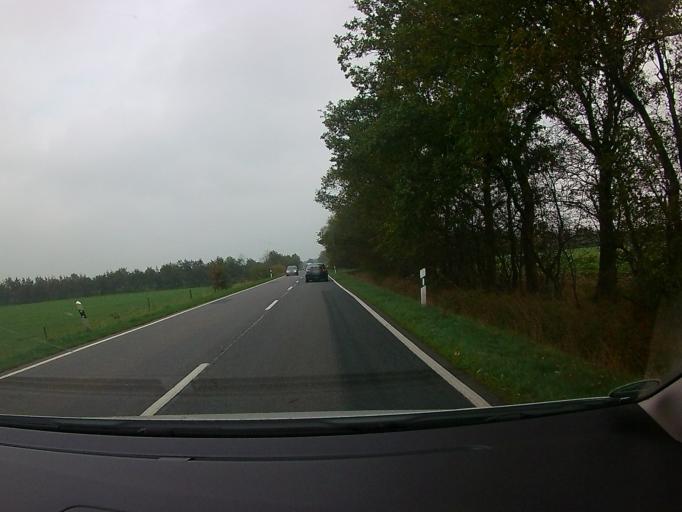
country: DE
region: Schleswig-Holstein
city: Wanderup
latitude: 54.6971
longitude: 9.3035
